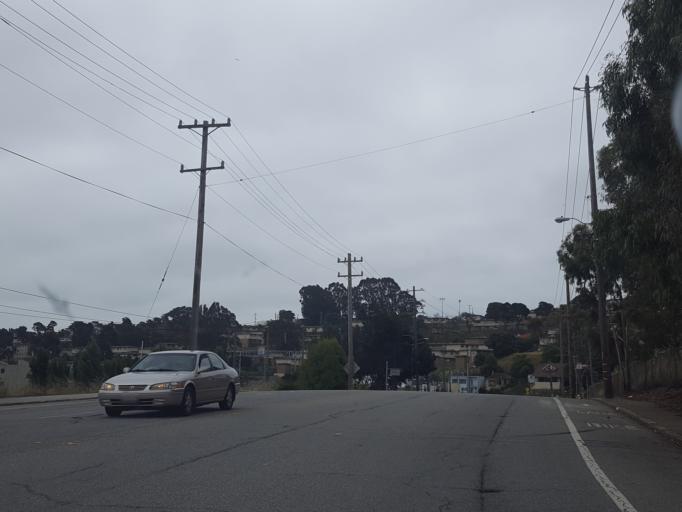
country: US
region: California
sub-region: San Francisco County
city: San Francisco
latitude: 37.7351
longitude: -122.3768
